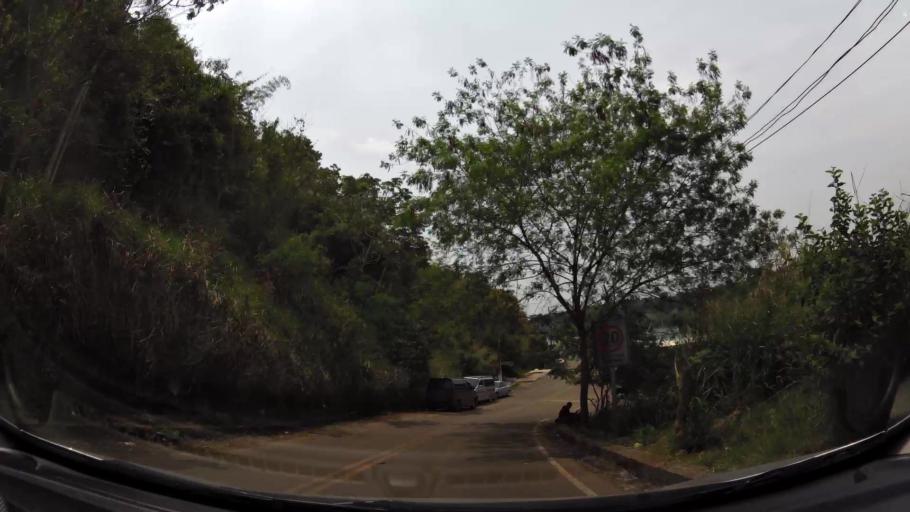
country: AR
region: Misiones
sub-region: Departamento de Iguazu
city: Puerto Iguazu
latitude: -25.5934
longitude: -54.5970
